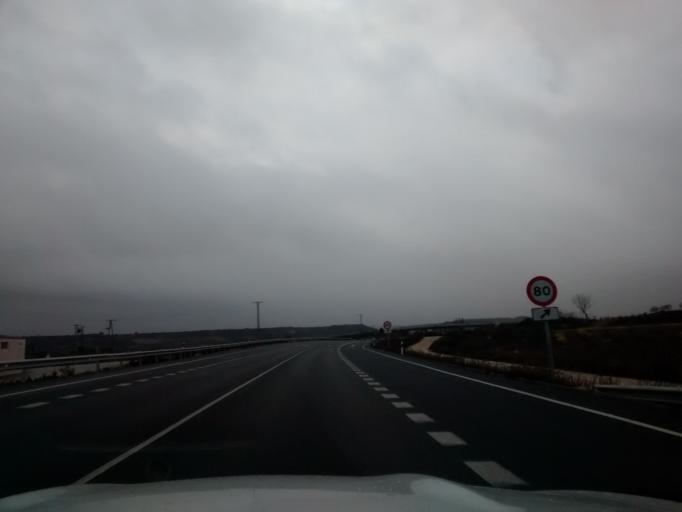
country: ES
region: La Rioja
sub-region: Provincia de La Rioja
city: San Asensio
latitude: 42.5117
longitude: -2.7359
